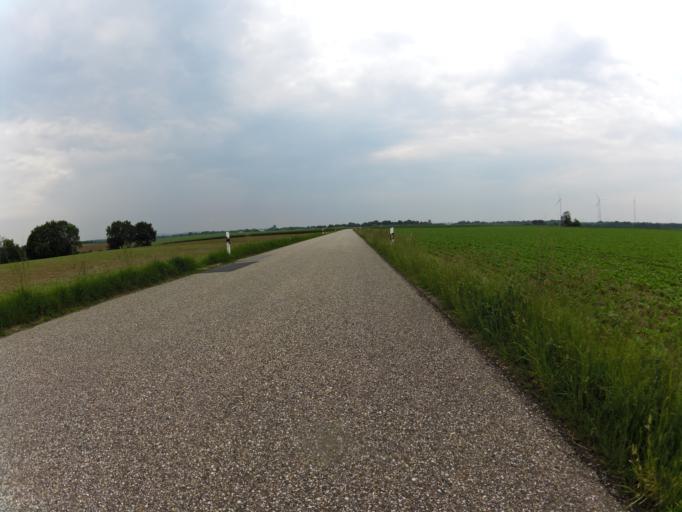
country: DE
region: North Rhine-Westphalia
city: Geilenkirchen
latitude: 50.9738
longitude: 6.1785
